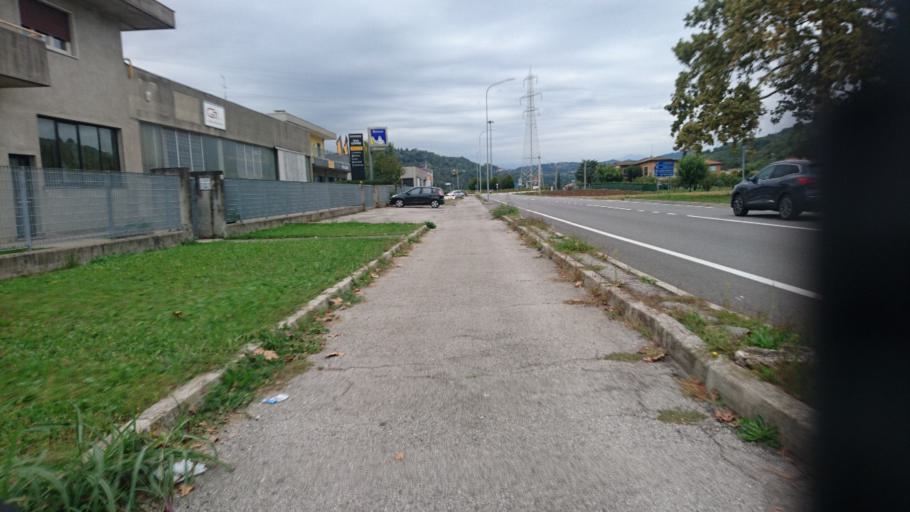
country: IT
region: Veneto
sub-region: Provincia di Vicenza
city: Sovizzo
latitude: 45.5279
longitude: 11.4527
